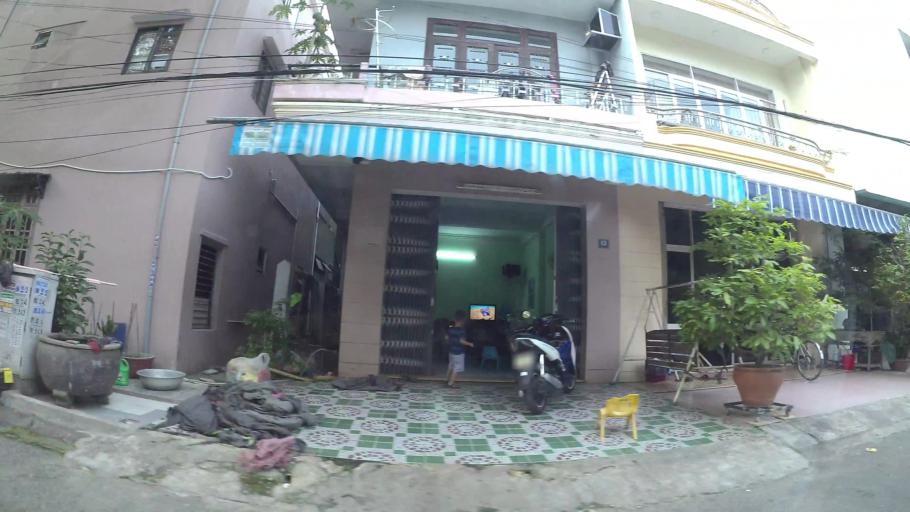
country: VN
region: Da Nang
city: Son Tra
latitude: 16.0536
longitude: 108.2357
